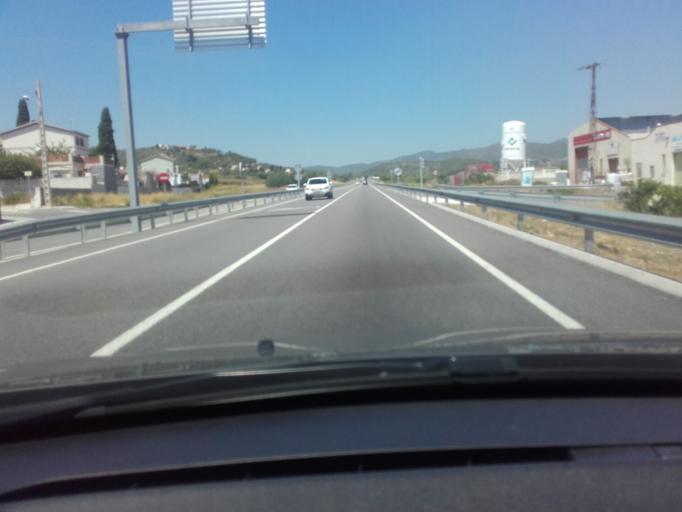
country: ES
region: Catalonia
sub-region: Provincia de Tarragona
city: Albinyana
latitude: 41.2560
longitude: 1.5041
